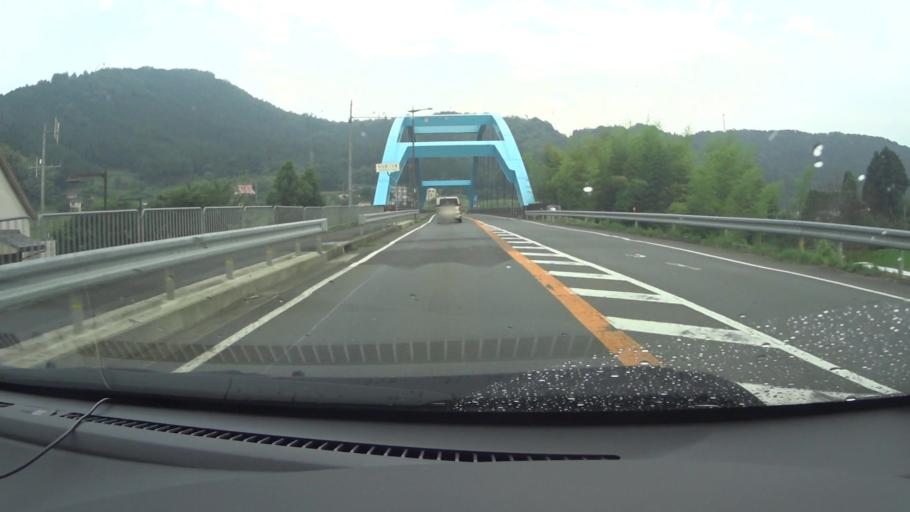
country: JP
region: Kyoto
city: Ayabe
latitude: 35.2696
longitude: 135.3974
